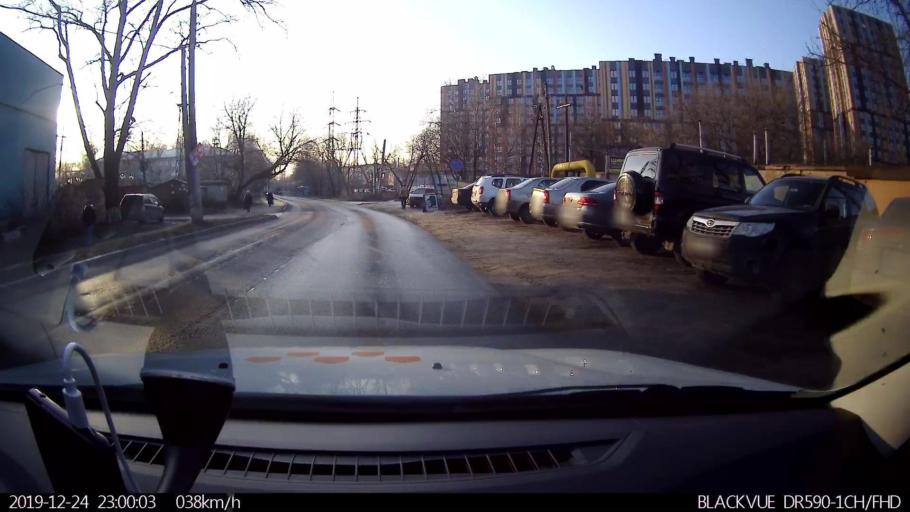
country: RU
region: Nizjnij Novgorod
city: Nizhniy Novgorod
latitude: 56.2735
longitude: 43.9349
